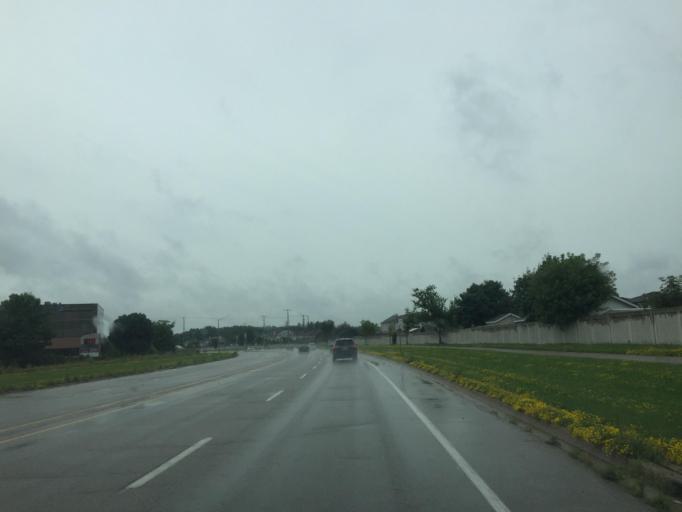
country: CA
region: Ontario
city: Cambridge
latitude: 43.3969
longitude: -80.2956
